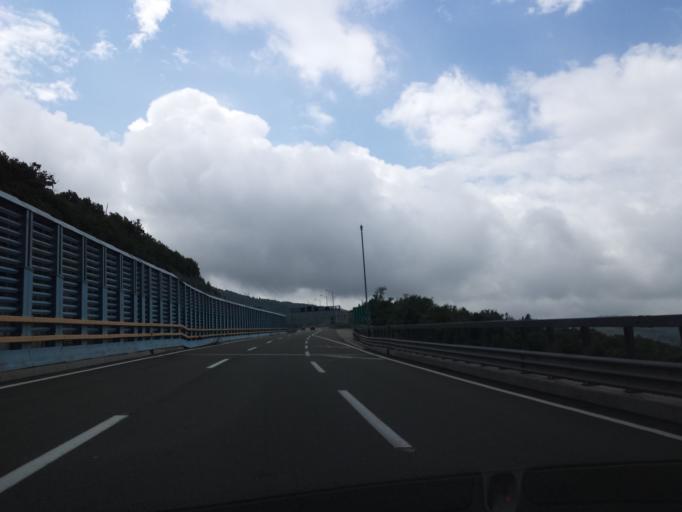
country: HR
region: Primorsko-Goranska
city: Hreljin
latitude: 45.3267
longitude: 14.6194
